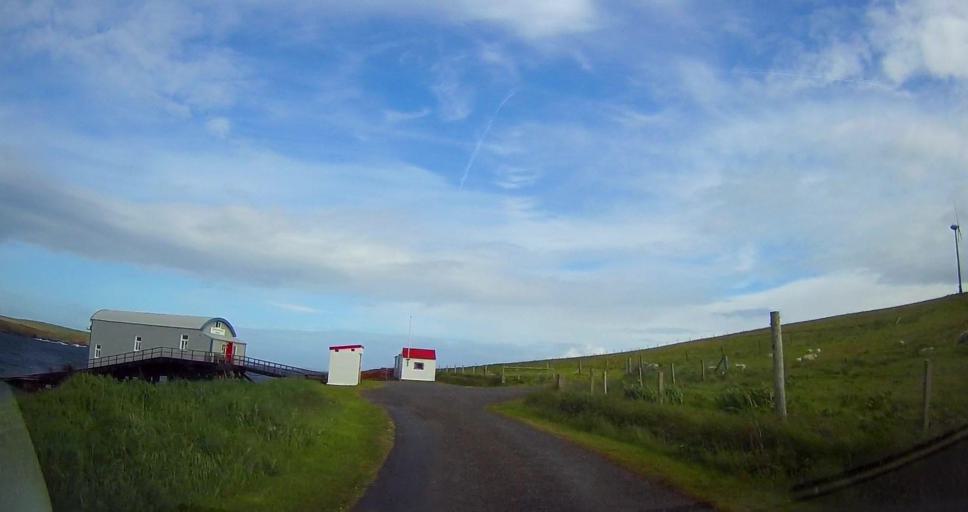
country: GB
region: Scotland
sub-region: Orkney Islands
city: Stromness
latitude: 58.7797
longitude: -3.2294
